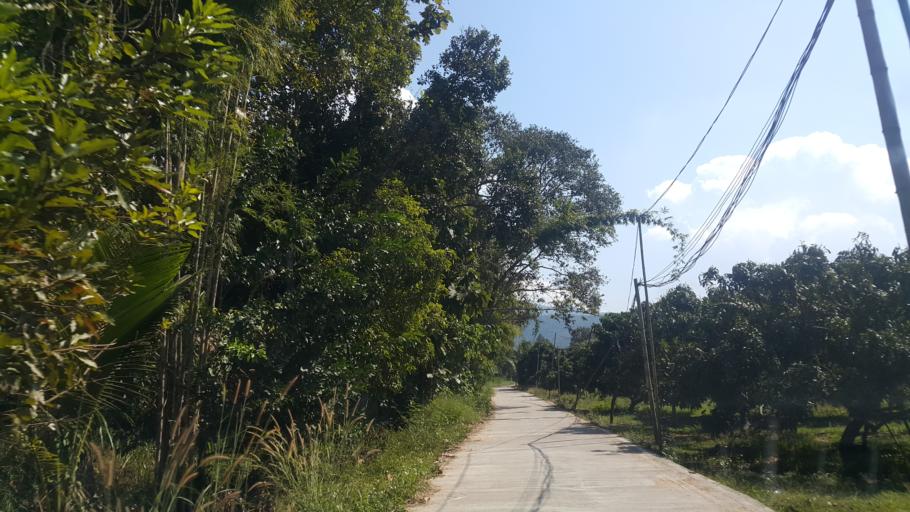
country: TH
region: Lamphun
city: Ban Thi
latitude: 18.6779
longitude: 99.1712
